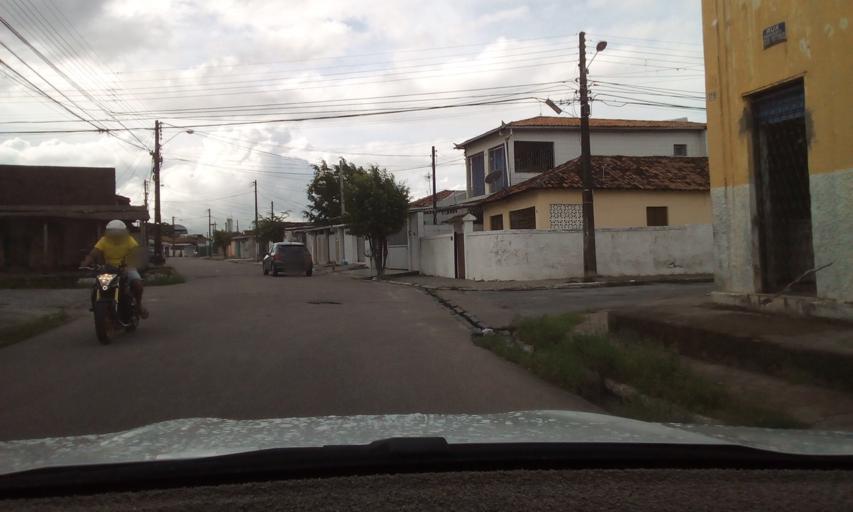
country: BR
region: Paraiba
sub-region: Joao Pessoa
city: Joao Pessoa
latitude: -7.1424
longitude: -34.8870
